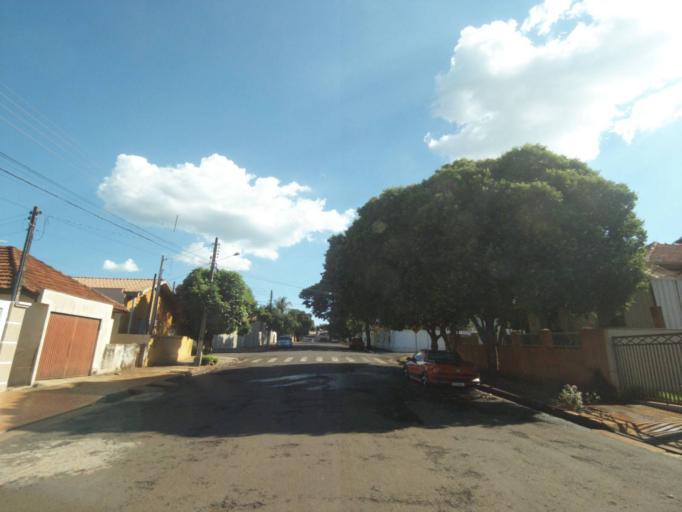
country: BR
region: Parana
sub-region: Sertanopolis
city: Sertanopolis
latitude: -23.0355
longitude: -50.8178
